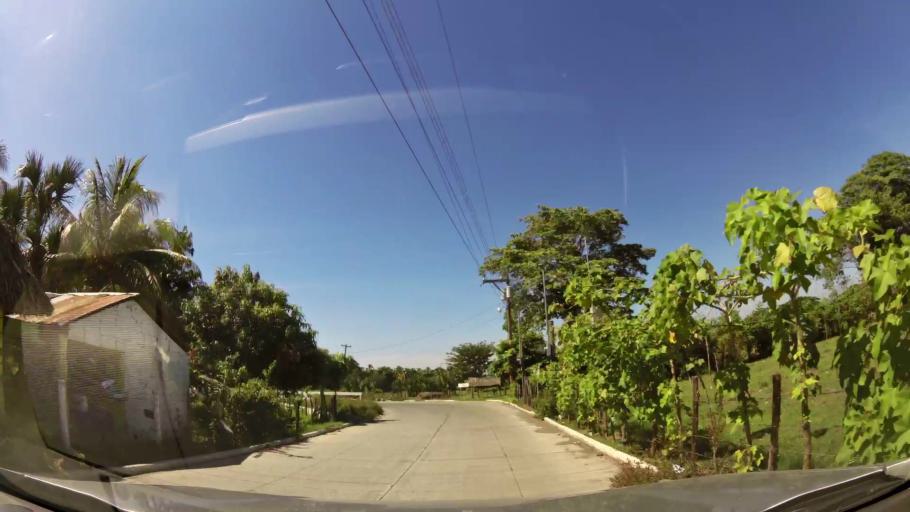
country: GT
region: Escuintla
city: Iztapa
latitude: 13.9389
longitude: -90.7047
